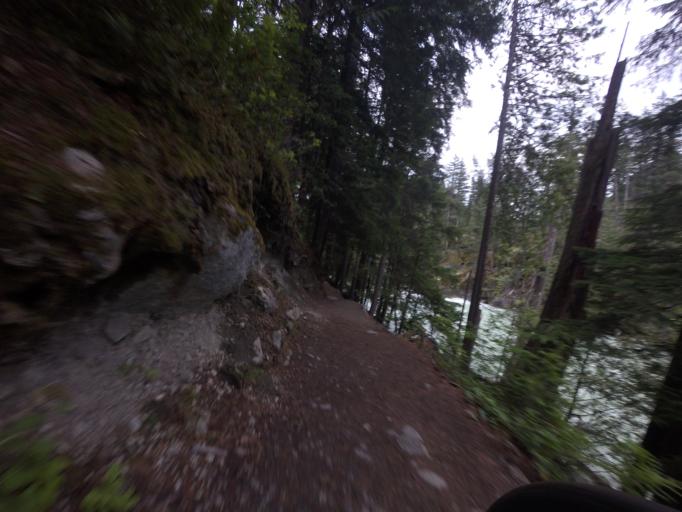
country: CA
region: British Columbia
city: Pemberton
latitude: 50.2936
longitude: -122.8262
